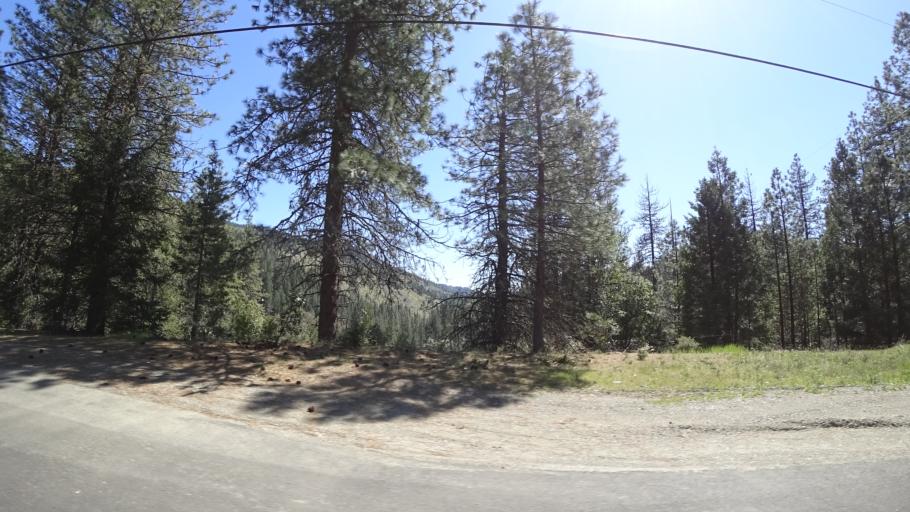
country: US
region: California
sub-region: Trinity County
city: Weaverville
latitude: 40.7500
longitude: -122.8890
